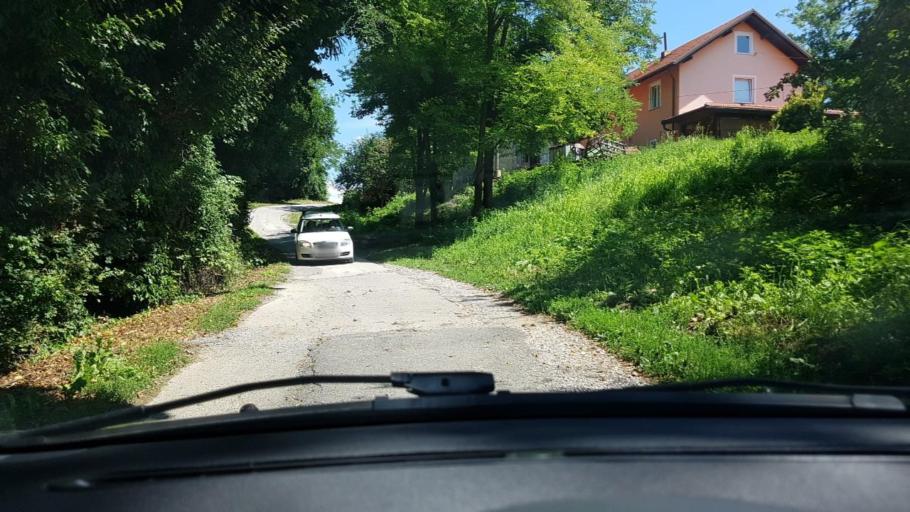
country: HR
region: Krapinsko-Zagorska
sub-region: Grad Krapina
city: Krapina
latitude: 46.1127
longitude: 15.8528
